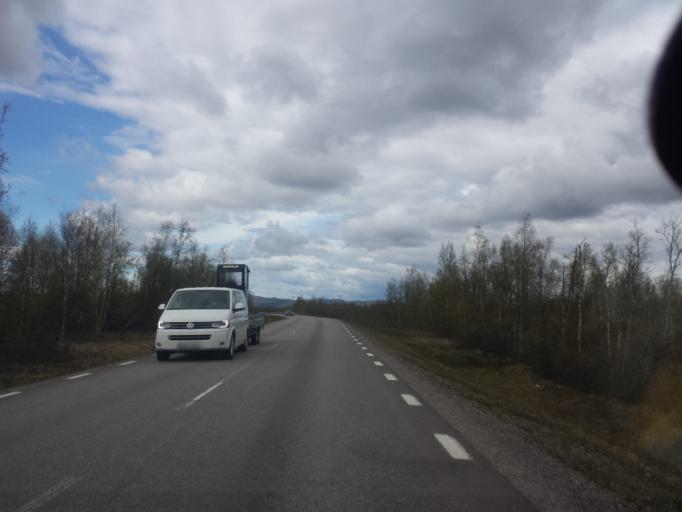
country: SE
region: Norrbotten
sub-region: Kiruna Kommun
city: Kiruna
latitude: 67.8924
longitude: 20.1306
